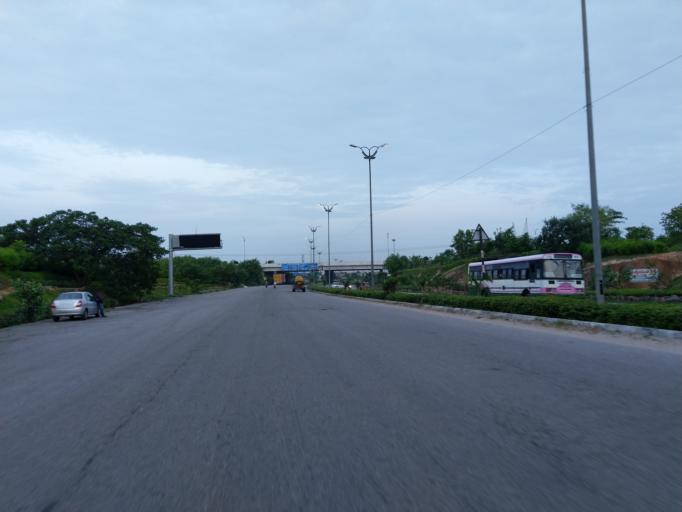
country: IN
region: Telangana
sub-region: Rangareddi
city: Lal Bahadur Nagar
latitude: 17.3172
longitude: 78.6601
